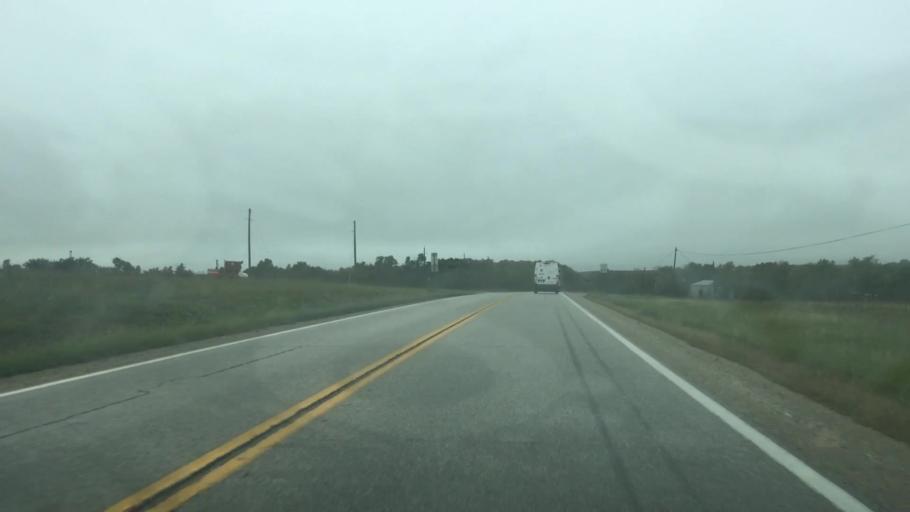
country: US
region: Kansas
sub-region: Anderson County
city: Garnett
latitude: 38.1952
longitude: -95.2516
